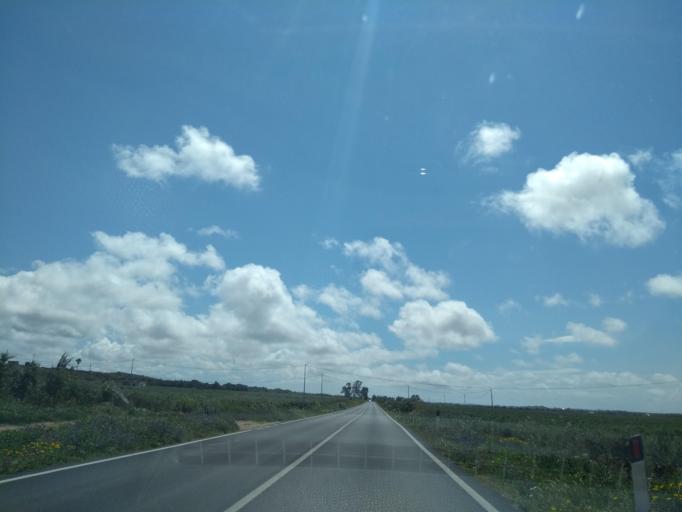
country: IT
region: Sicily
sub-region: Trapani
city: Rilievo
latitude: 37.9017
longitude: 12.5305
